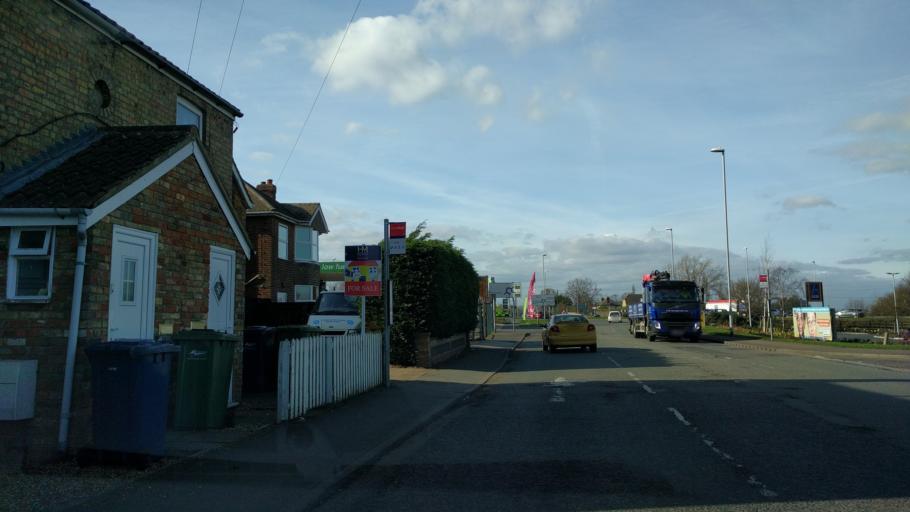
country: GB
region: England
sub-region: Cambridgeshire
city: Chatteris
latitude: 52.4638
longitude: 0.0447
